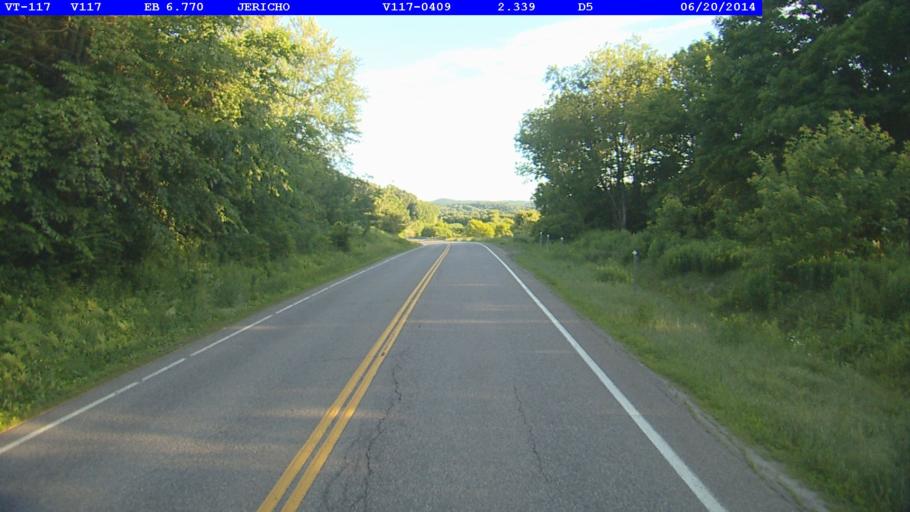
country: US
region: Vermont
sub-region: Chittenden County
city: Williston
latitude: 44.4420
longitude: -73.0195
